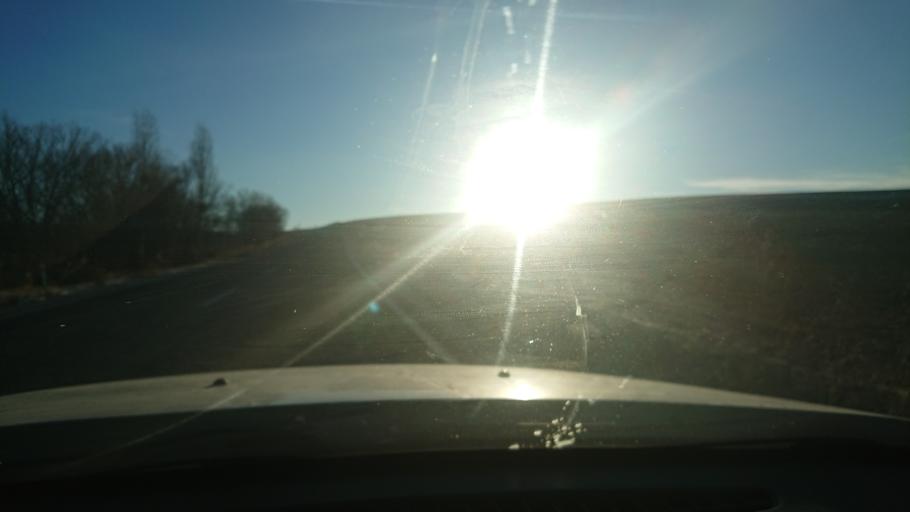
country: TR
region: Aksaray
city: Agacoren
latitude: 38.8508
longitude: 33.8986
